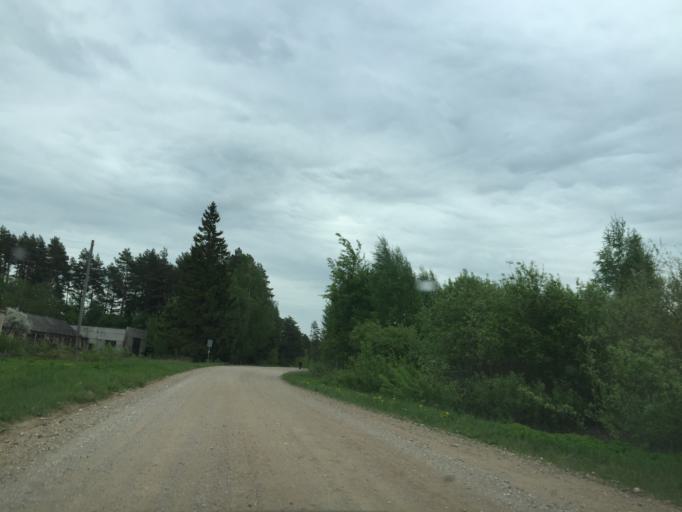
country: LV
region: Lielvarde
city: Lielvarde
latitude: 56.8051
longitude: 24.8444
